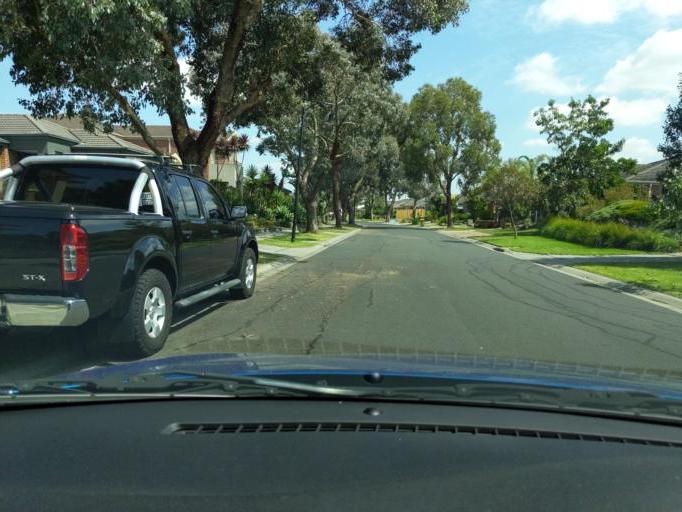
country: AU
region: Victoria
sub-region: Knox
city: Ferntree Gully
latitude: -37.8971
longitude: 145.2804
